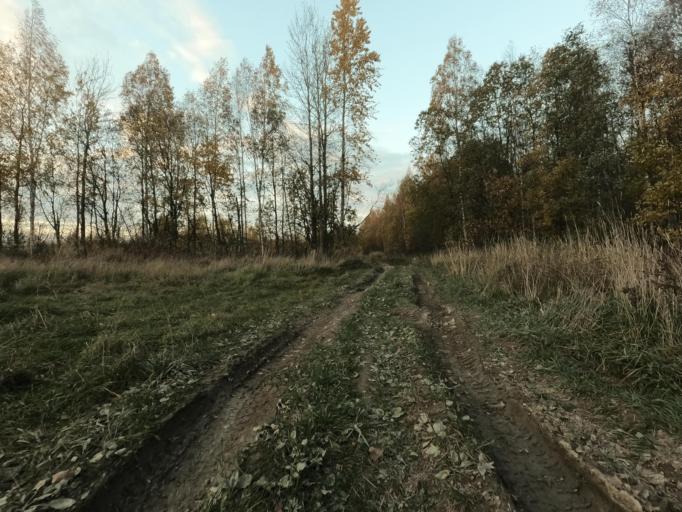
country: RU
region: Leningrad
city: Mga
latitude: 59.8138
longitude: 31.1778
